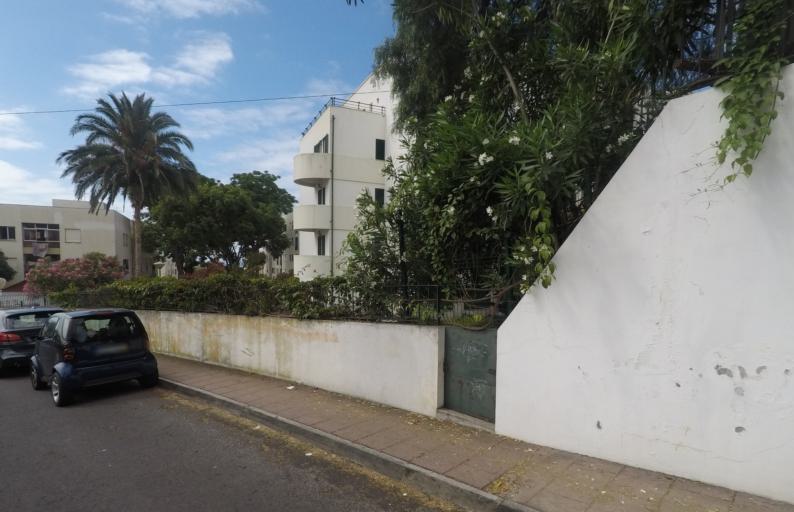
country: PT
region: Madeira
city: Camara de Lobos
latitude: 32.6468
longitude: -16.9343
